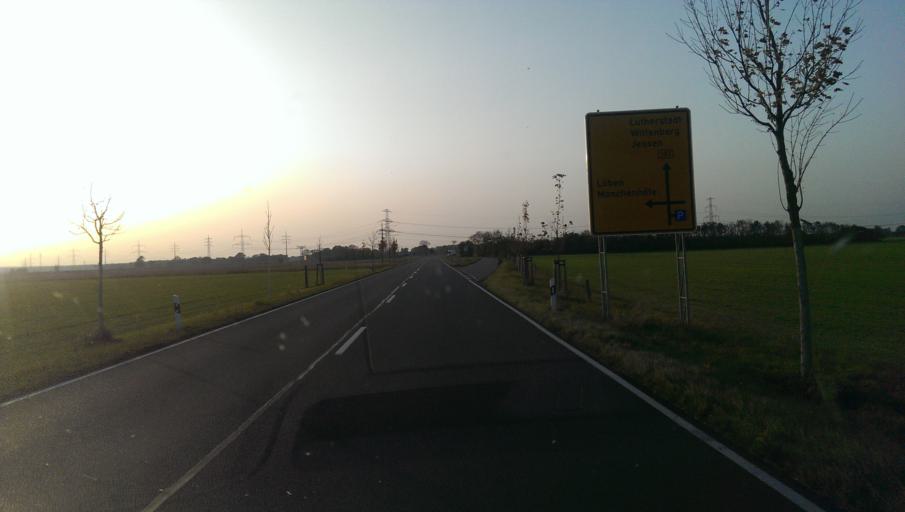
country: DE
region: Saxony-Anhalt
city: Annaburg
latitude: 51.7877
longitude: 13.0598
